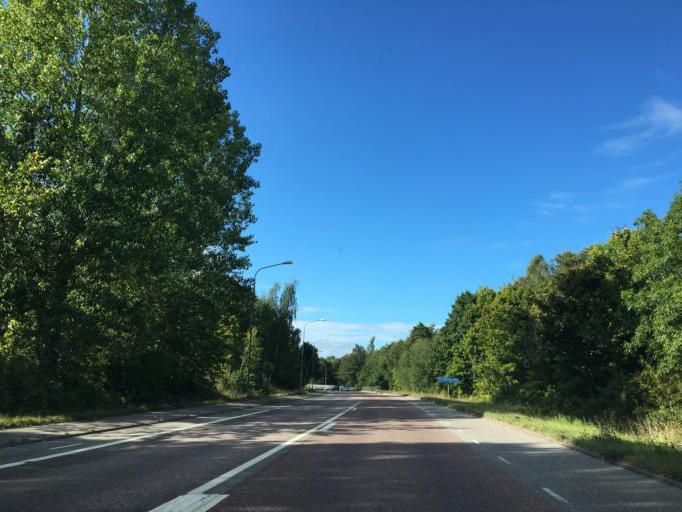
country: SE
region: Soedermanland
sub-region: Nykopings Kommun
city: Nykoping
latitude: 58.7737
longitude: 16.9828
